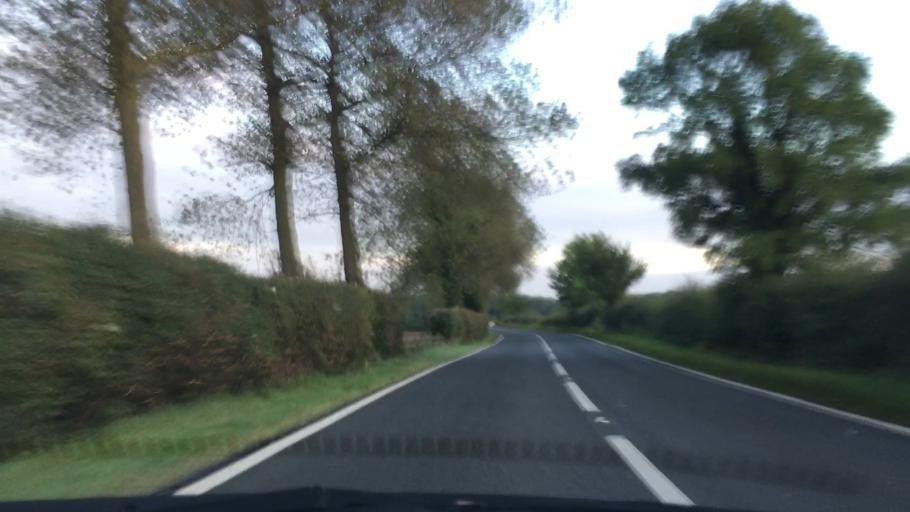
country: GB
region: England
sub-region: North East Lincolnshire
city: Wold Newton
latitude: 53.4594
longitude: -0.0922
